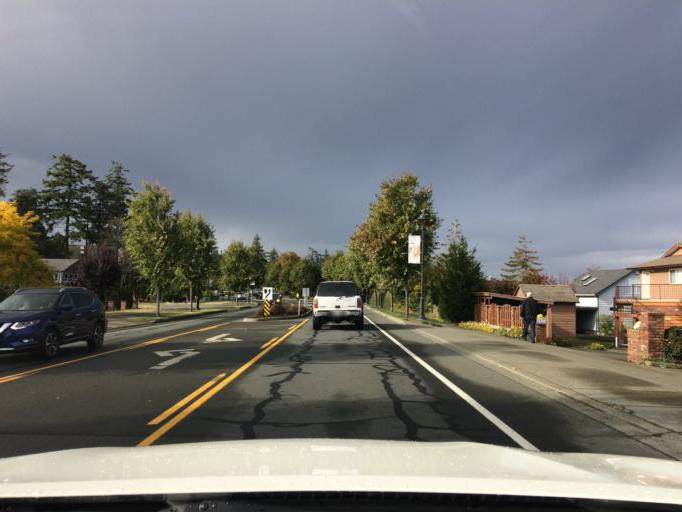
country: CA
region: British Columbia
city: Campbell River
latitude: 49.9683
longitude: -125.2101
